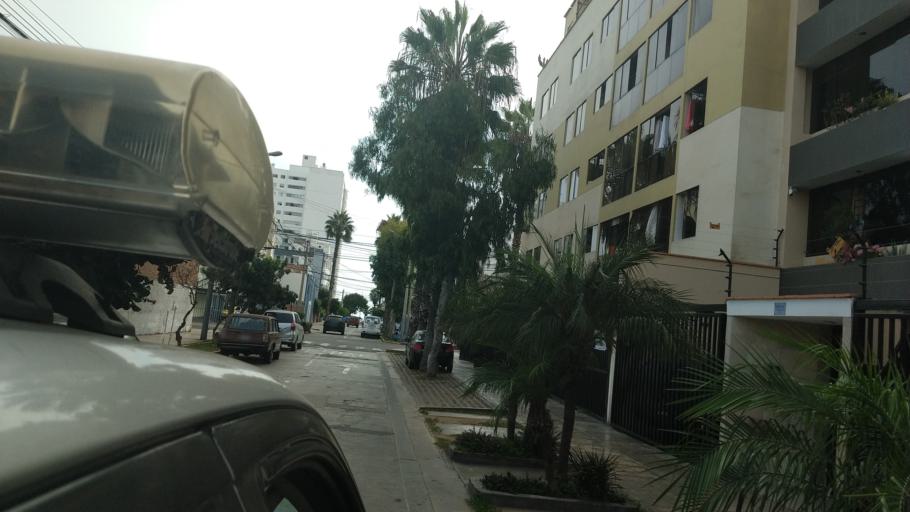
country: PE
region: Lima
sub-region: Lima
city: San Isidro
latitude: -12.0914
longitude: -77.0782
